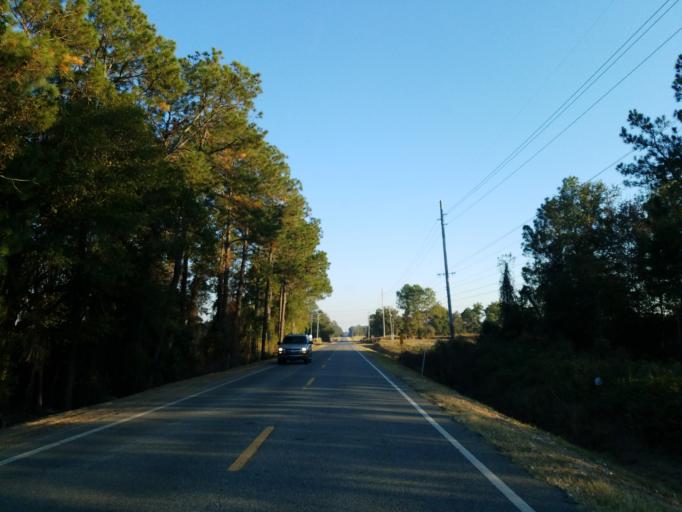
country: US
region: Georgia
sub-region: Crisp County
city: Cordele
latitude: 31.9016
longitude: -83.6965
